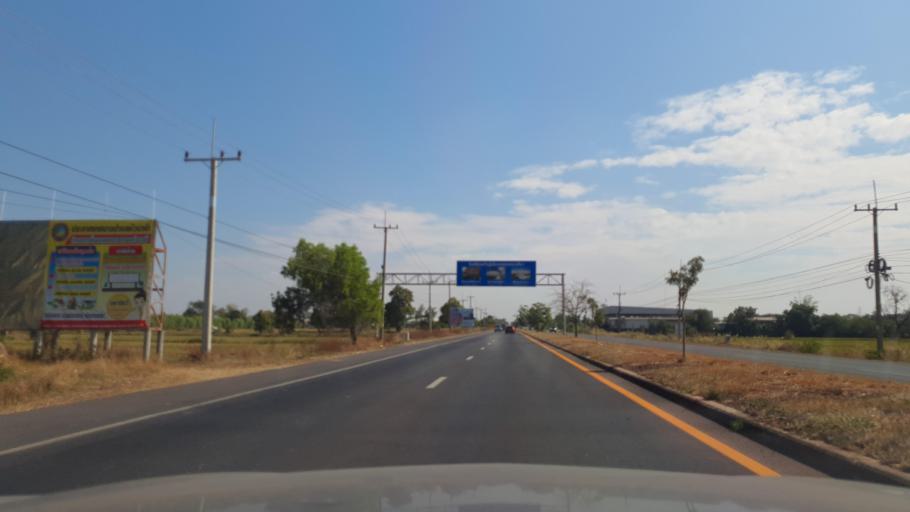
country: TH
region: Maha Sarakham
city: Chiang Yuen
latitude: 16.3764
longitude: 103.1709
